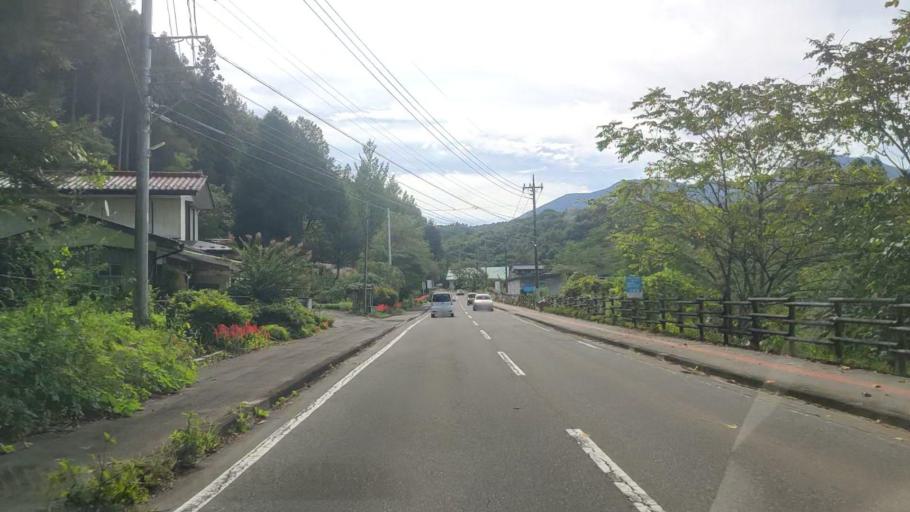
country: JP
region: Gunma
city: Nakanojomachi
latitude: 36.6234
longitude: 138.9278
